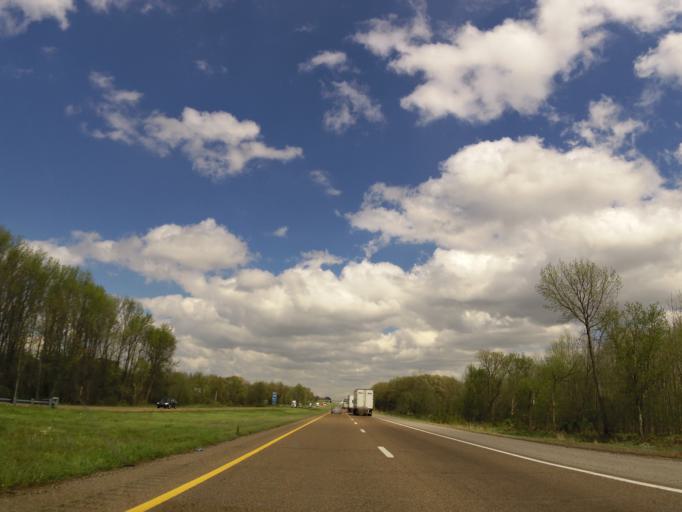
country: US
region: Tennessee
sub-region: Tipton County
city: Mason
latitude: 35.3424
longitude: -89.5322
